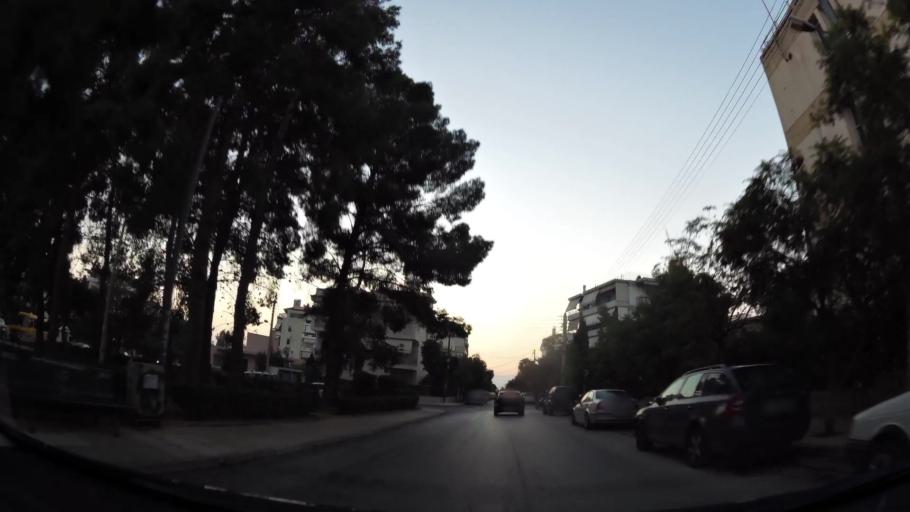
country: GR
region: Attica
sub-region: Nomarchia Athinas
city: Argyroupoli
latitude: 37.8894
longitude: 23.7553
